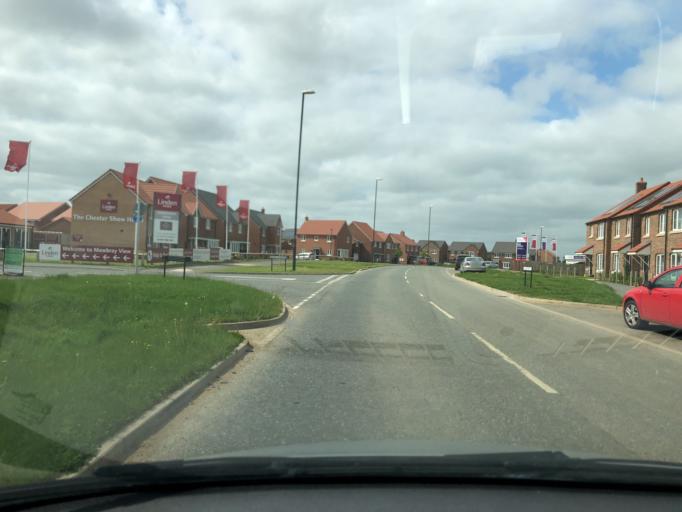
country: GB
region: England
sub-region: North Yorkshire
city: Thirsk
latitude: 54.2203
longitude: -1.3534
